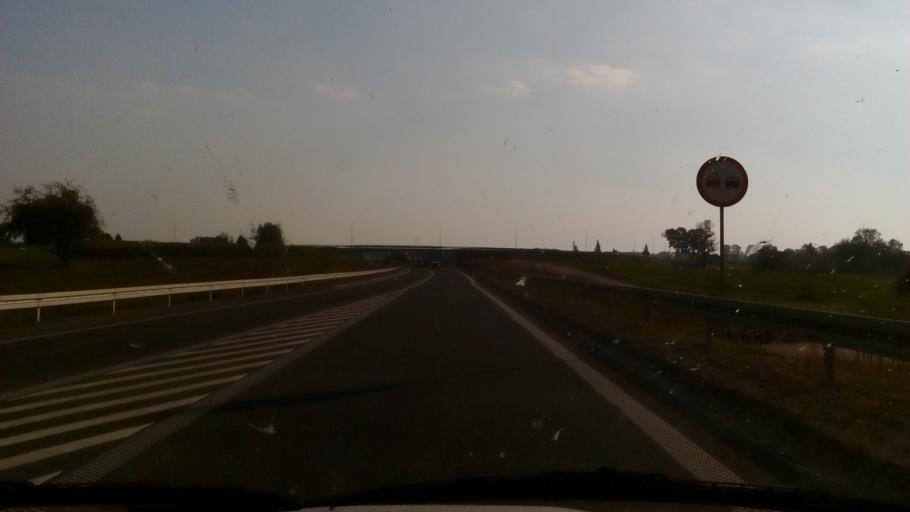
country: PL
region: Podlasie
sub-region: Powiat grajewski
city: Rajgrod
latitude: 53.7768
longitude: 22.8364
